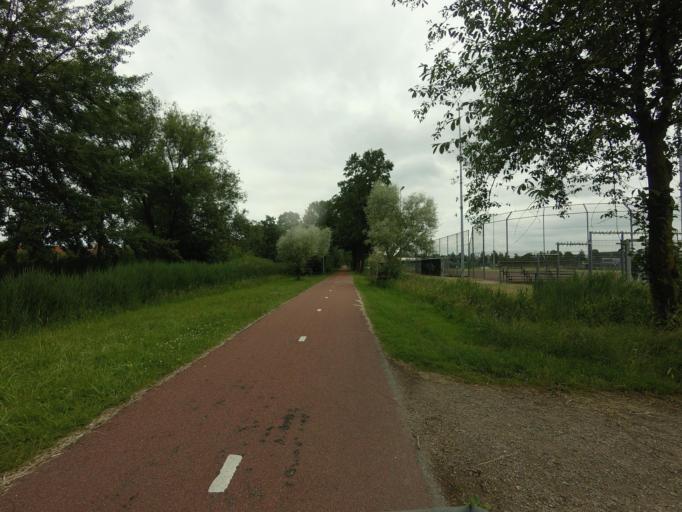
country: NL
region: North Holland
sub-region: Gemeente Huizen
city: Huizen
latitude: 52.2928
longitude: 5.2701
